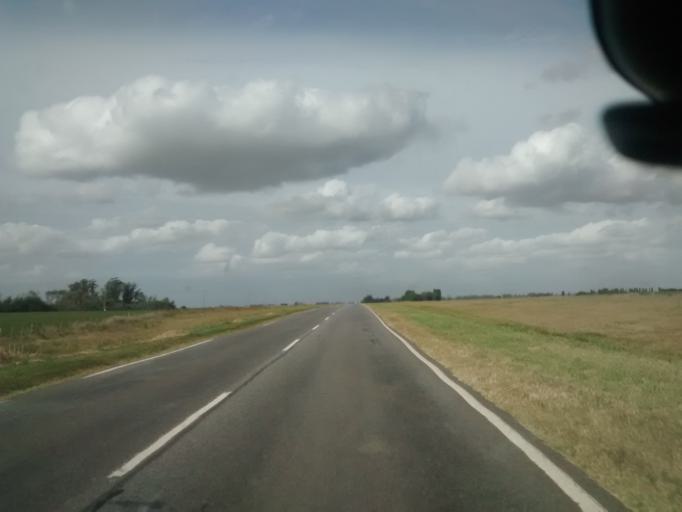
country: AR
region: Buenos Aires
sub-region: Partido de Balcarce
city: Balcarce
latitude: -37.6696
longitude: -58.5262
